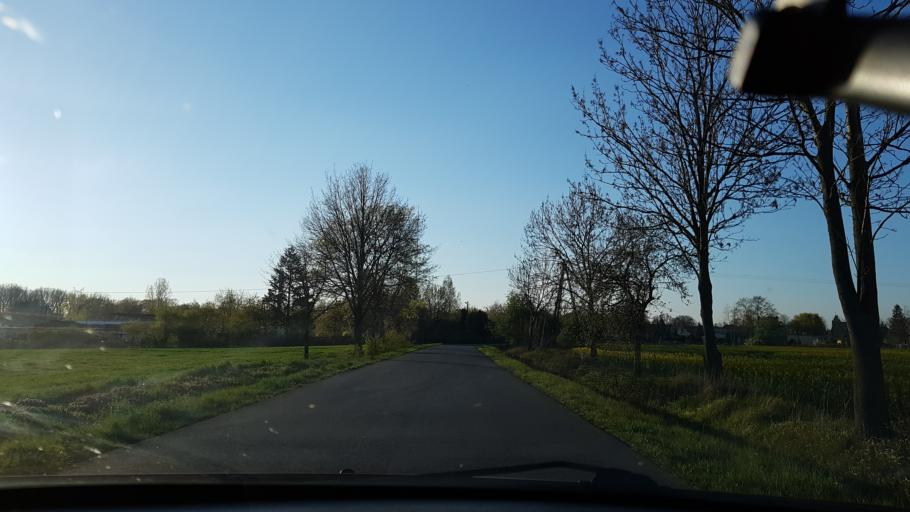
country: PL
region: Opole Voivodeship
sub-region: Powiat nyski
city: Nysa
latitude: 50.4273
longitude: 17.3084
